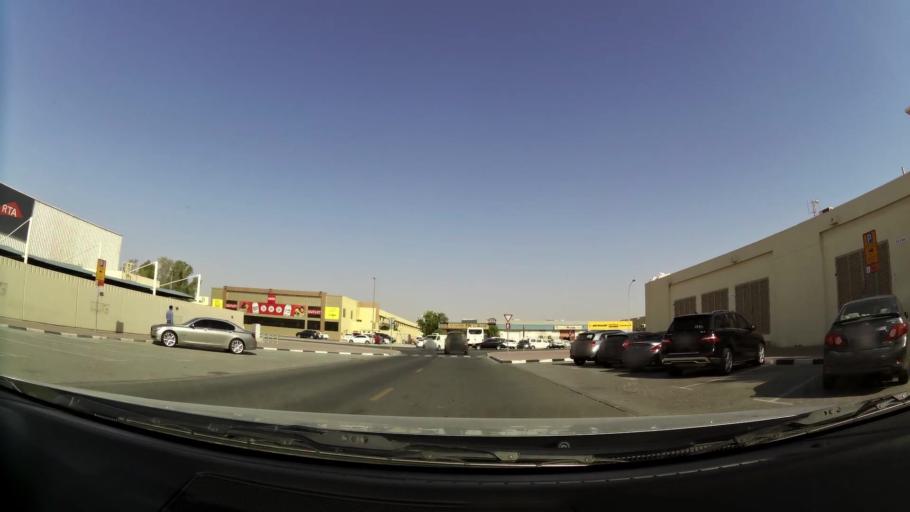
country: AE
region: Dubai
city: Dubai
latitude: 25.1266
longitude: 55.2101
